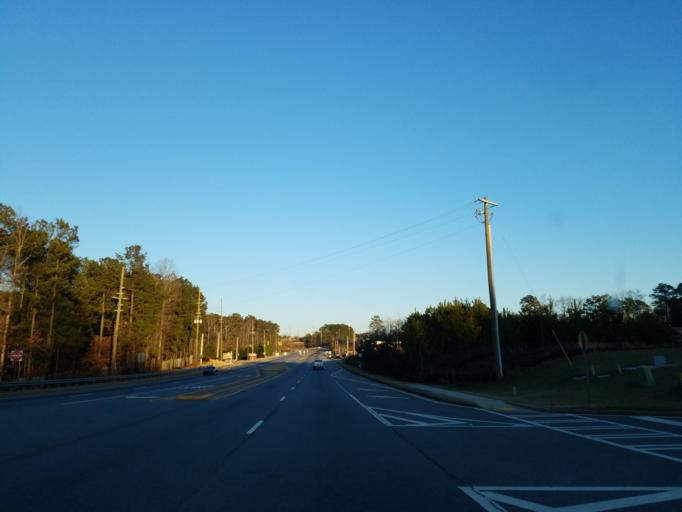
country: US
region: Georgia
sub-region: Cherokee County
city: Woodstock
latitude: 34.1133
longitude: -84.5715
